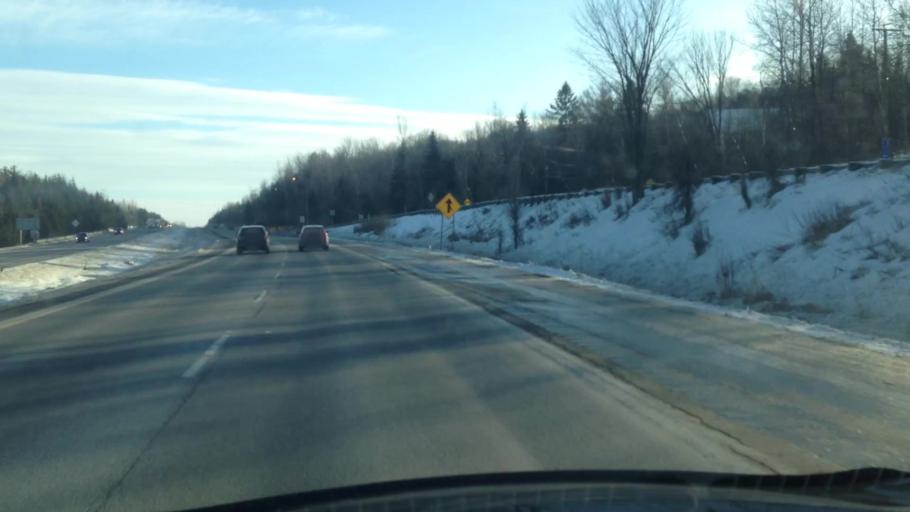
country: CA
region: Quebec
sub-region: Laurentides
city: Prevost
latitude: 45.8659
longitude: -74.0857
